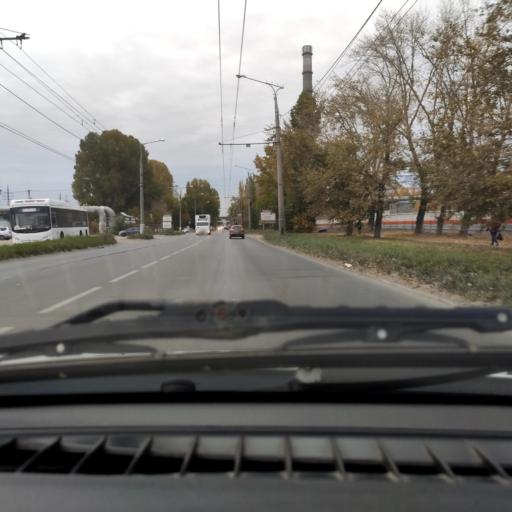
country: RU
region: Samara
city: Tol'yatti
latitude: 53.5464
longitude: 49.4464
